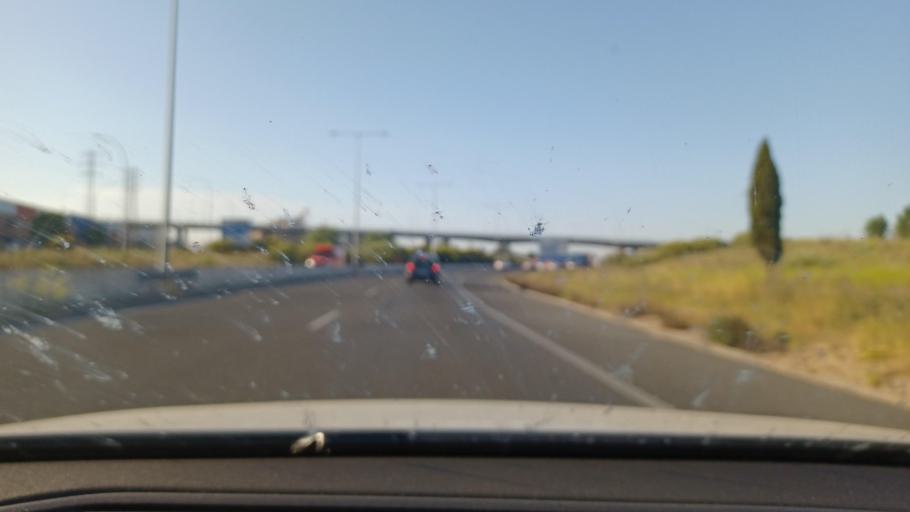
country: ES
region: Castille and Leon
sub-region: Provincia de Valladolid
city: Cisterniga
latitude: 41.6152
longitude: -4.7134
